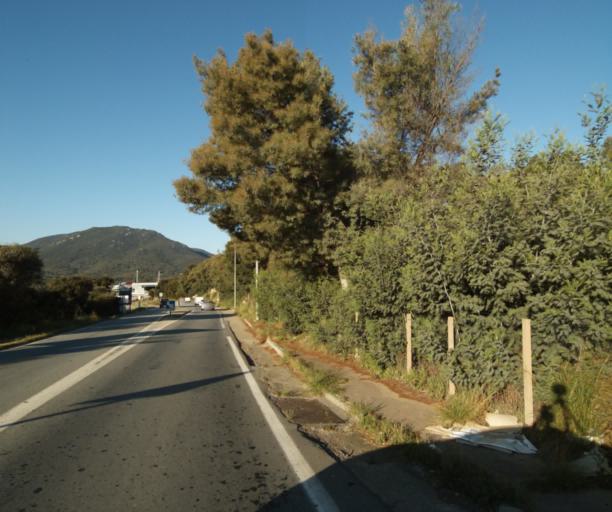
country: FR
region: Corsica
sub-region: Departement de la Corse-du-Sud
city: Propriano
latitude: 41.6666
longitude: 8.9208
